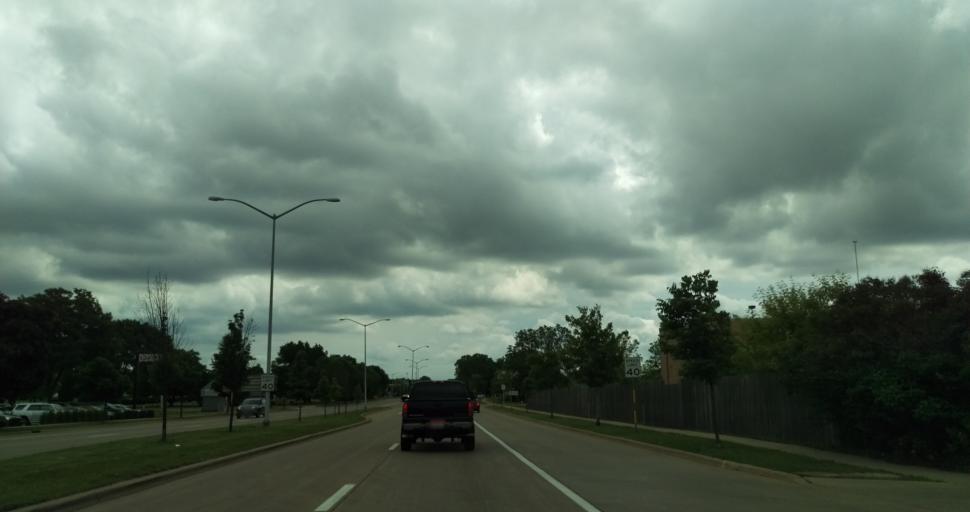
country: US
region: Wisconsin
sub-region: Dane County
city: Middleton
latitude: 43.0606
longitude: -89.5120
